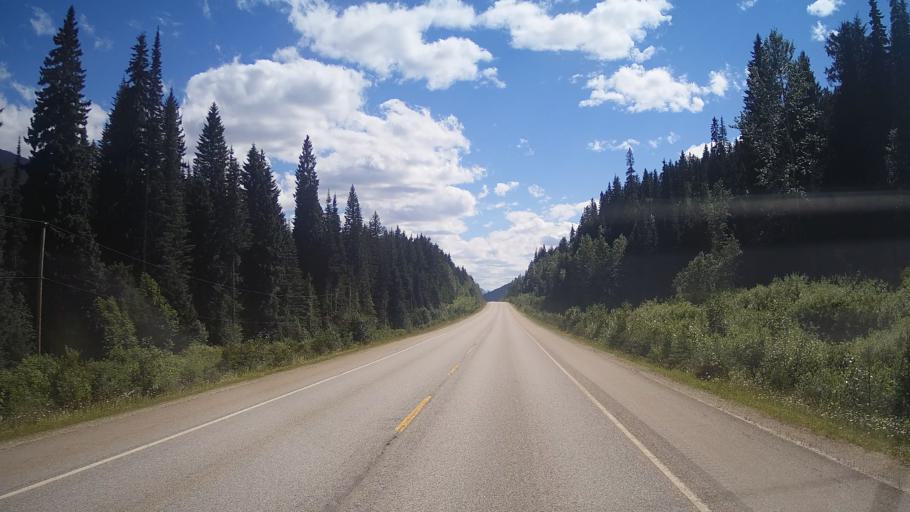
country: CA
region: Alberta
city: Jasper Park Lodge
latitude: 52.5589
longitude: -119.1102
